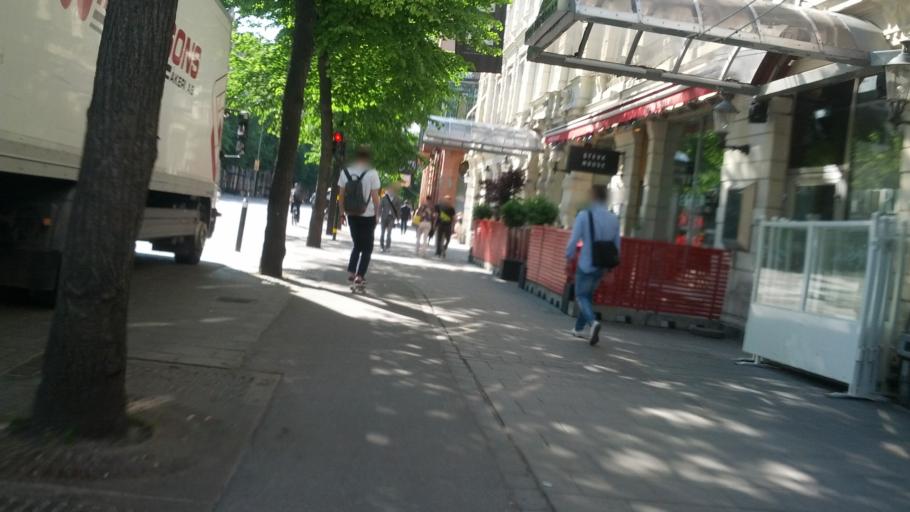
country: SE
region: Stockholm
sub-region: Stockholms Kommun
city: Stockholm
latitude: 59.3379
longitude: 18.0696
